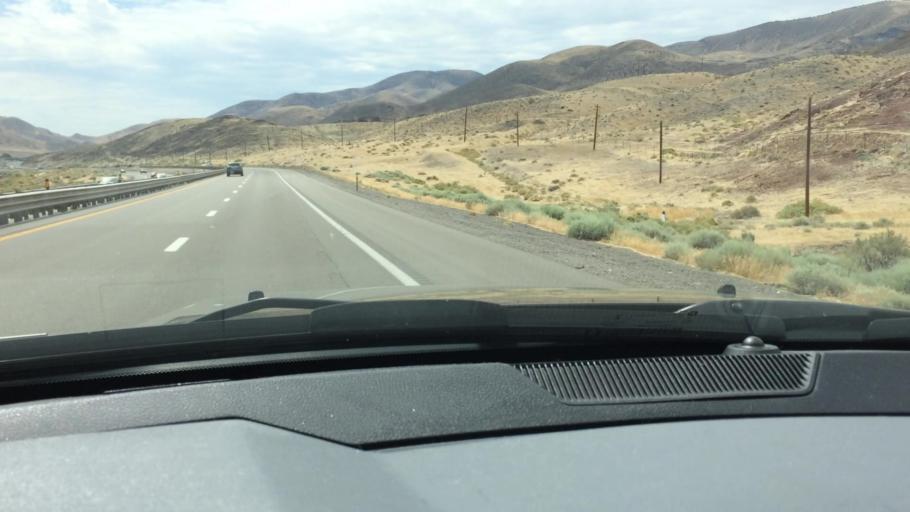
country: US
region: Nevada
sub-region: Lyon County
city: Fernley
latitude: 39.5914
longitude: -119.4101
